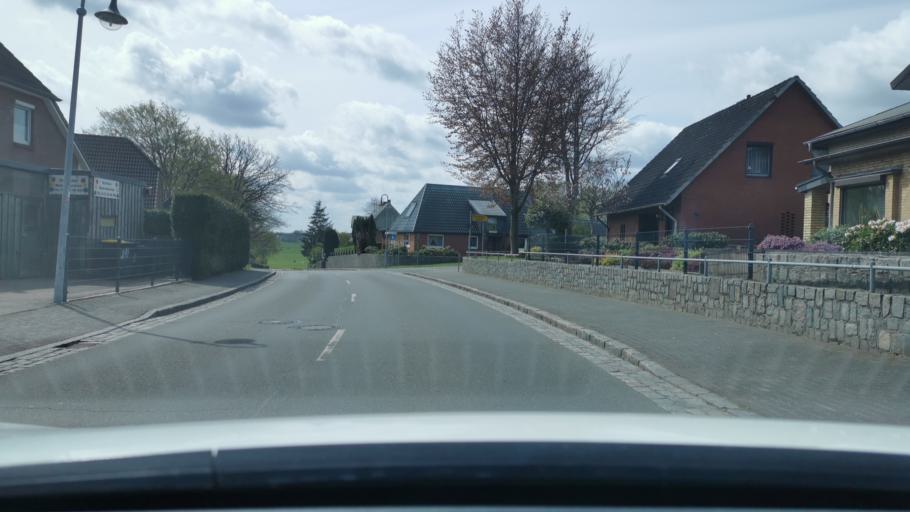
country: DE
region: Schleswig-Holstein
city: Hamdorf
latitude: 54.2204
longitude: 9.5184
